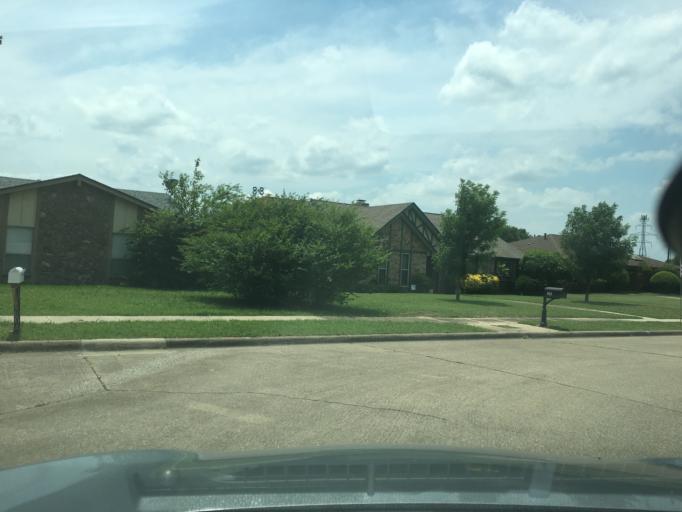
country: US
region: Texas
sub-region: Dallas County
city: Richardson
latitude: 32.9566
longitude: -96.6961
